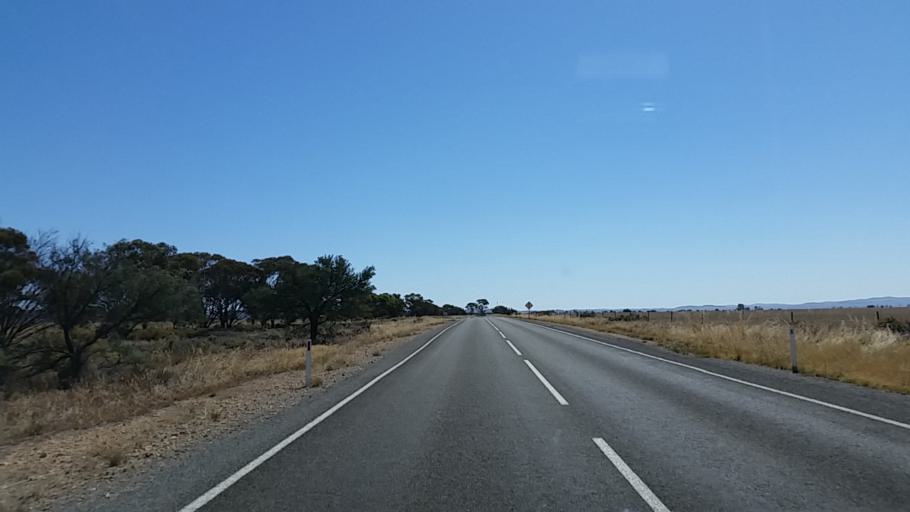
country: AU
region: South Australia
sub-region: Peterborough
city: Peterborough
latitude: -32.7521
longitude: 138.6414
